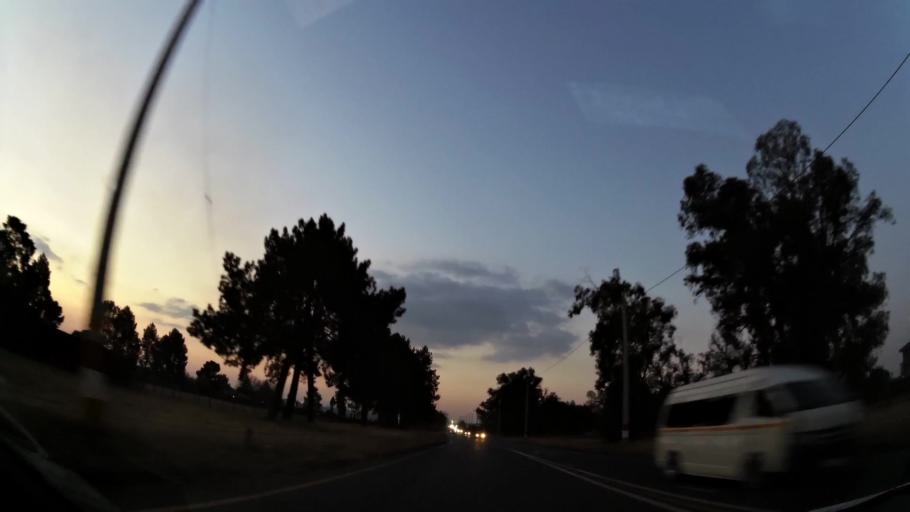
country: ZA
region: Gauteng
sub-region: Ekurhuleni Metropolitan Municipality
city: Springs
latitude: -26.2891
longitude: 28.4537
